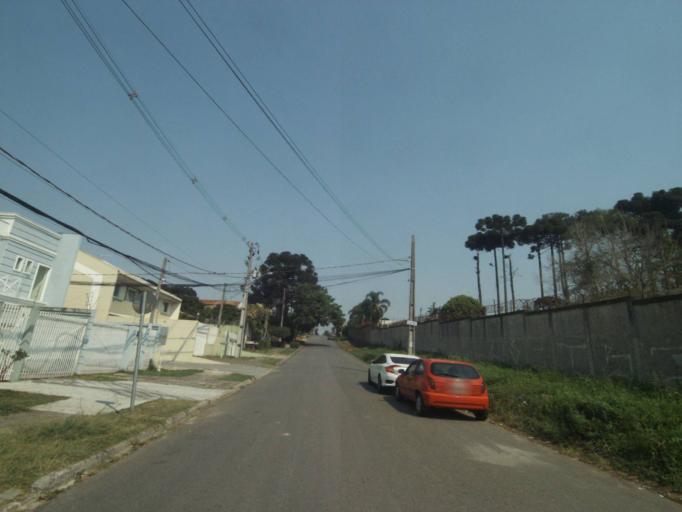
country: BR
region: Parana
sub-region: Sao Jose Dos Pinhais
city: Sao Jose dos Pinhais
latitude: -25.5197
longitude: -49.2501
